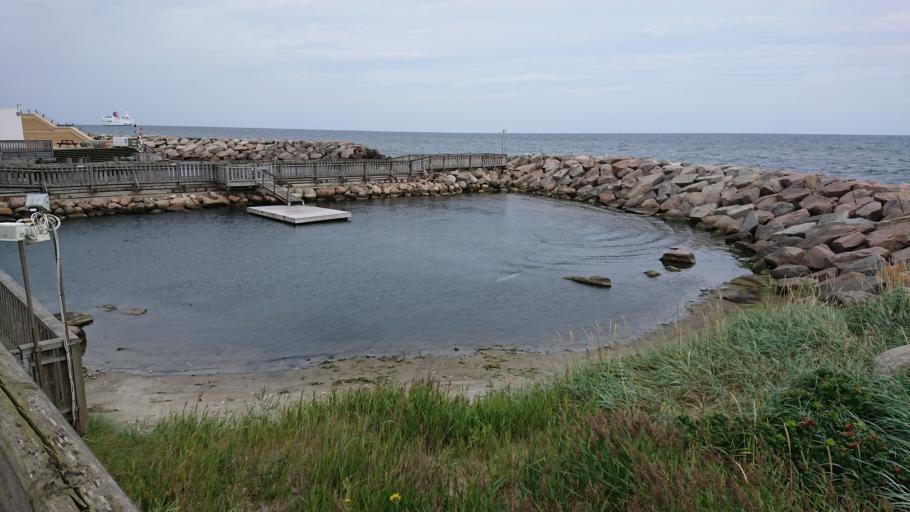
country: DK
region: Central Jutland
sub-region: Norddjurs Kommune
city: Grenaa
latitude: 56.4056
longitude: 10.9269
